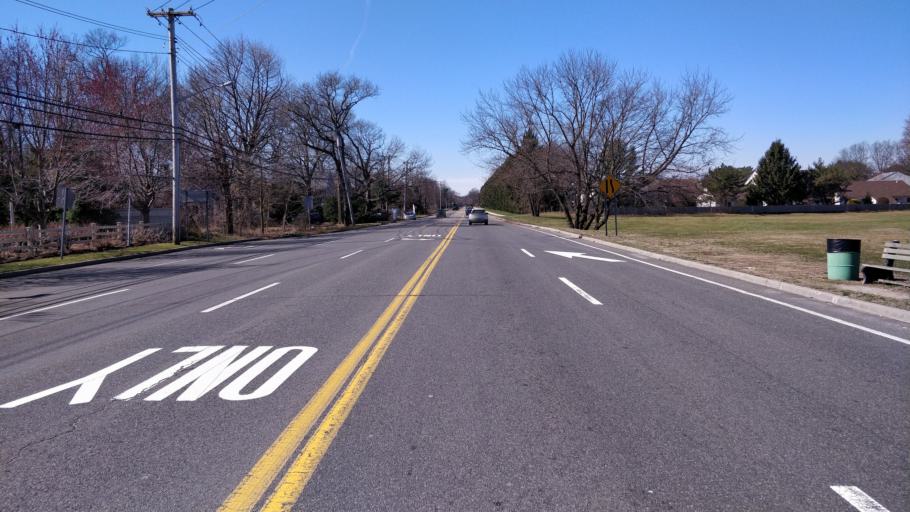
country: US
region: New York
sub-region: Suffolk County
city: Huntington Station
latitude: 40.8561
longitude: -73.3910
